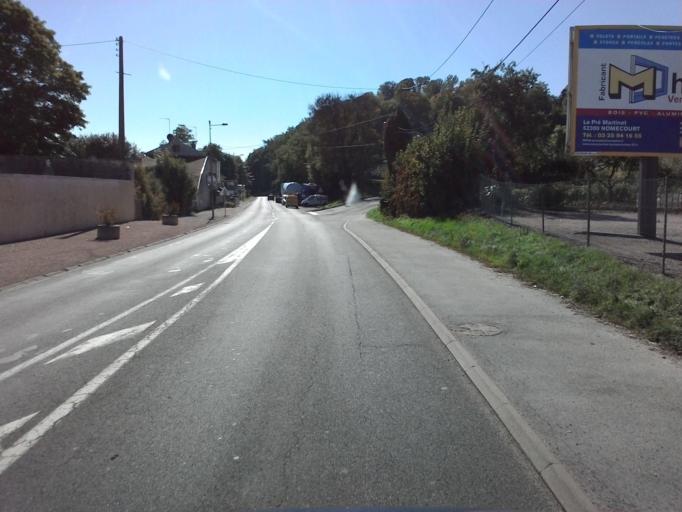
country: FR
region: Champagne-Ardenne
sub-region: Departement de la Haute-Marne
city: Chaumont
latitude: 48.1193
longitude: 5.1492
